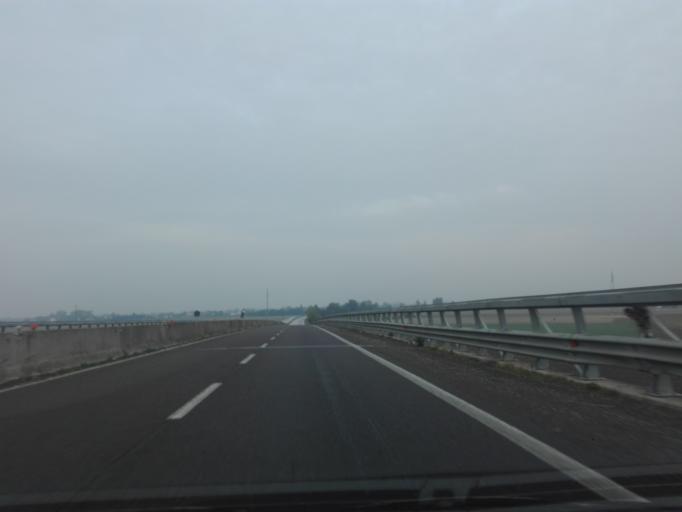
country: IT
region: Veneto
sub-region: Provincia di Rovigo
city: Grignano Polesine
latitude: 45.0253
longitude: 11.7575
